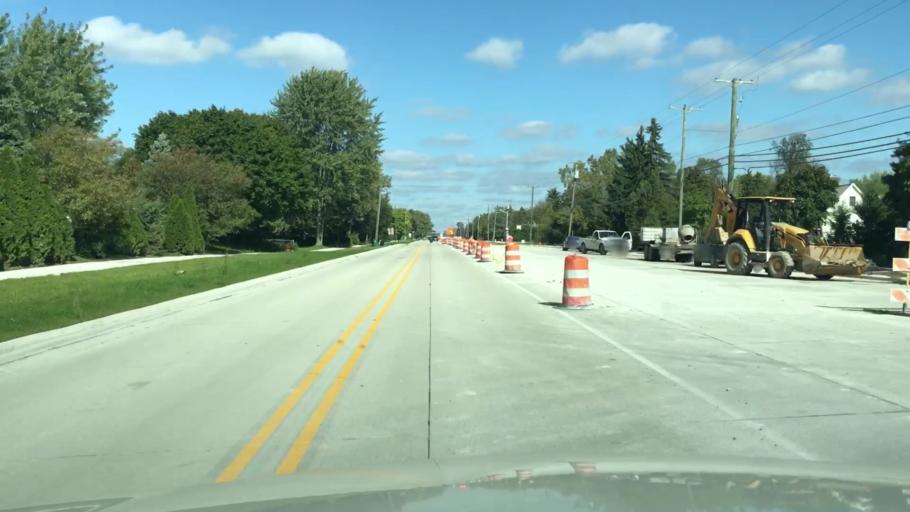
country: US
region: Michigan
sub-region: Oakland County
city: Troy
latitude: 42.5984
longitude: -83.0902
